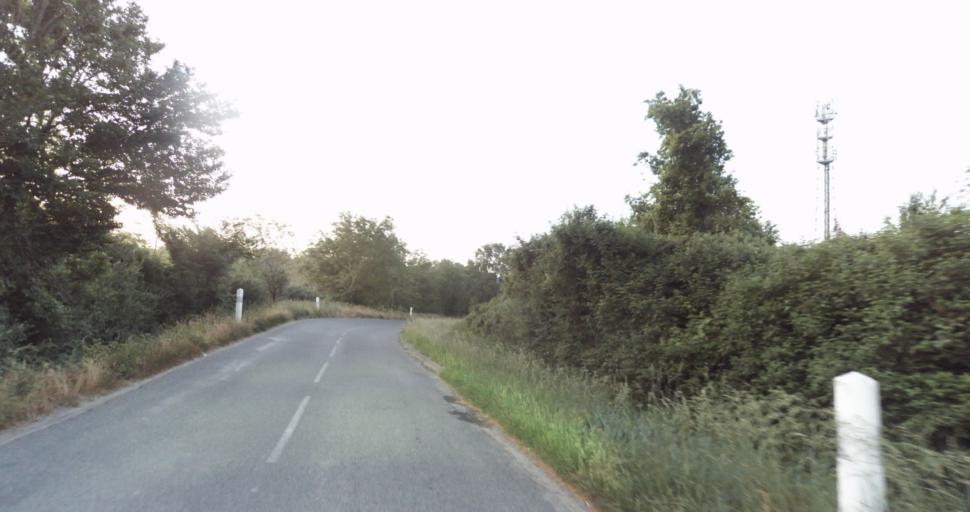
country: FR
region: Midi-Pyrenees
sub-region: Departement de la Haute-Garonne
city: Levignac
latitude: 43.6702
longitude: 1.1894
